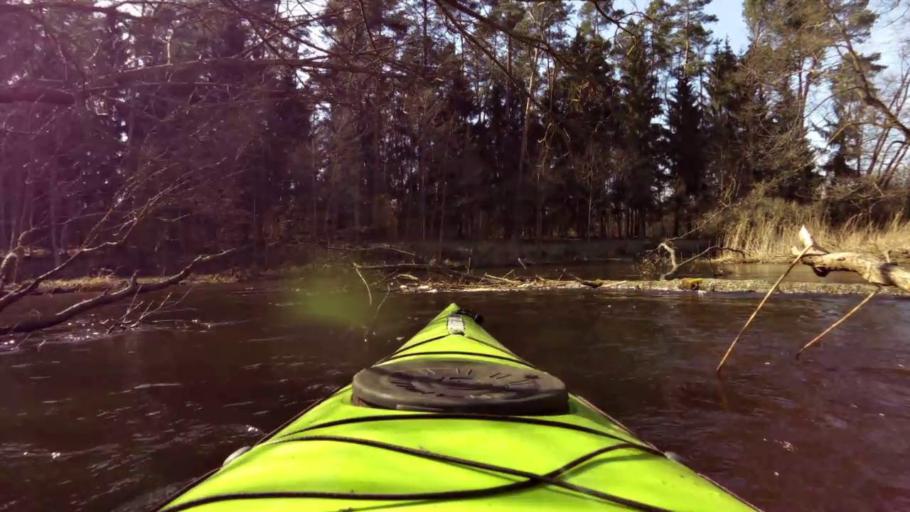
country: PL
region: West Pomeranian Voivodeship
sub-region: Powiat lobeski
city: Lobez
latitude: 53.6854
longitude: 15.5618
